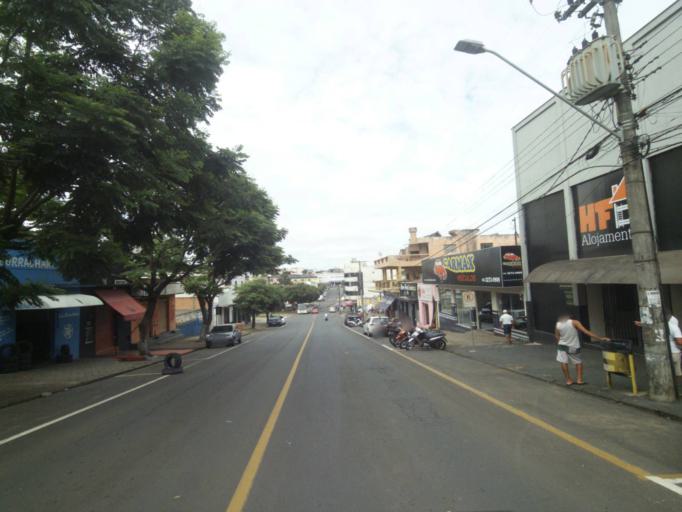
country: BR
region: Parana
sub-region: Telemaco Borba
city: Telemaco Borba
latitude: -24.3218
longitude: -50.6191
